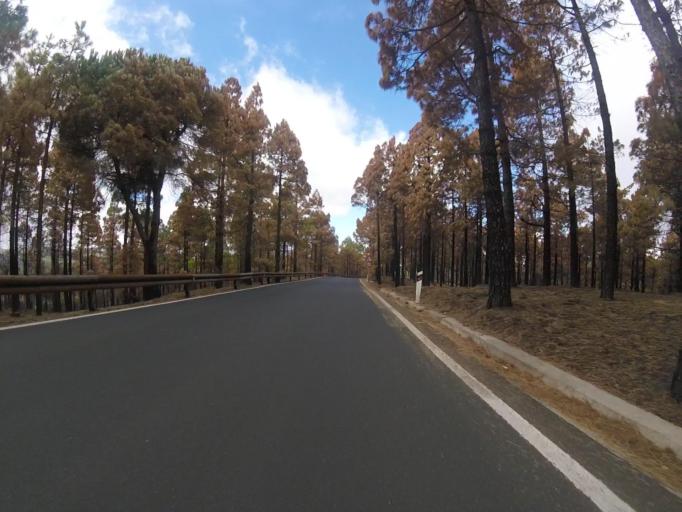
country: ES
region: Canary Islands
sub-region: Provincia de Las Palmas
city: Tejeda
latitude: 27.9736
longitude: -15.5781
